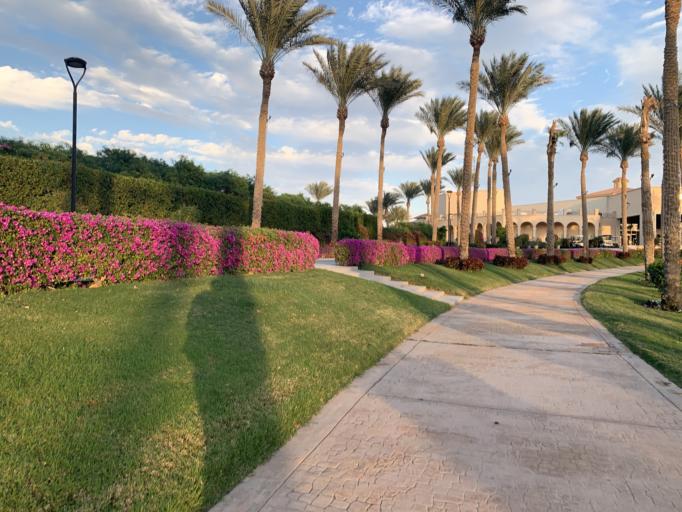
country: EG
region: South Sinai
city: Sharm el-Sheikh
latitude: 28.0219
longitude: 34.4362
